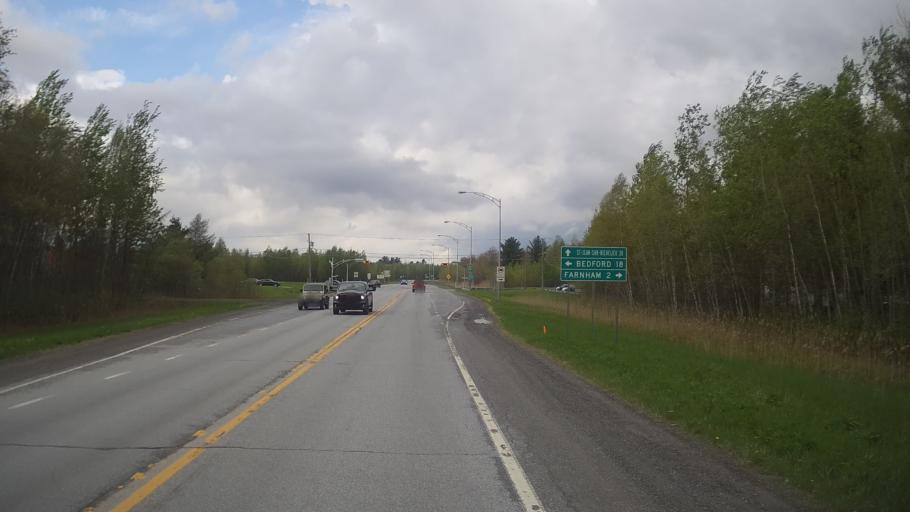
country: CA
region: Quebec
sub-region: Monteregie
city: Farnham
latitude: 45.2737
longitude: -72.9816
